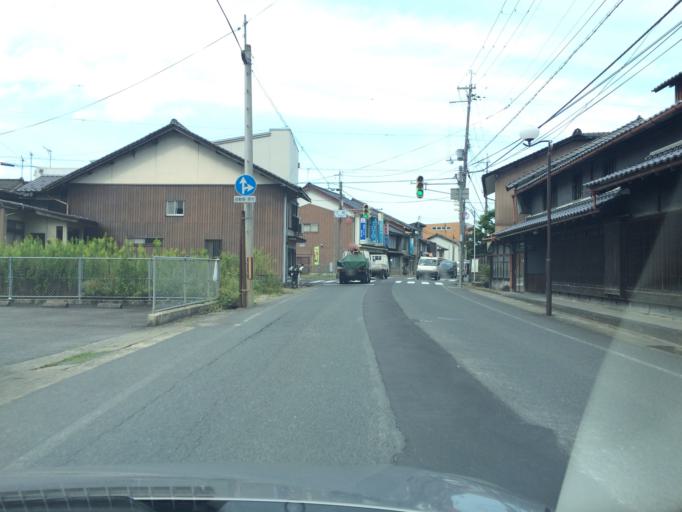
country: JP
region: Hyogo
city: Toyooka
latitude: 35.4665
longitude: 134.7756
